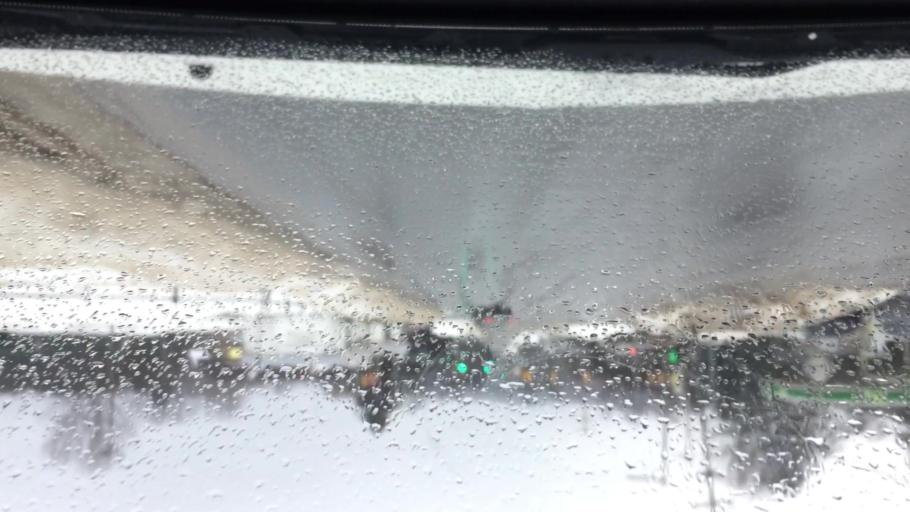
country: US
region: Michigan
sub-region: Charlevoix County
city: East Jordan
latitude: 45.1542
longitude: -85.1388
